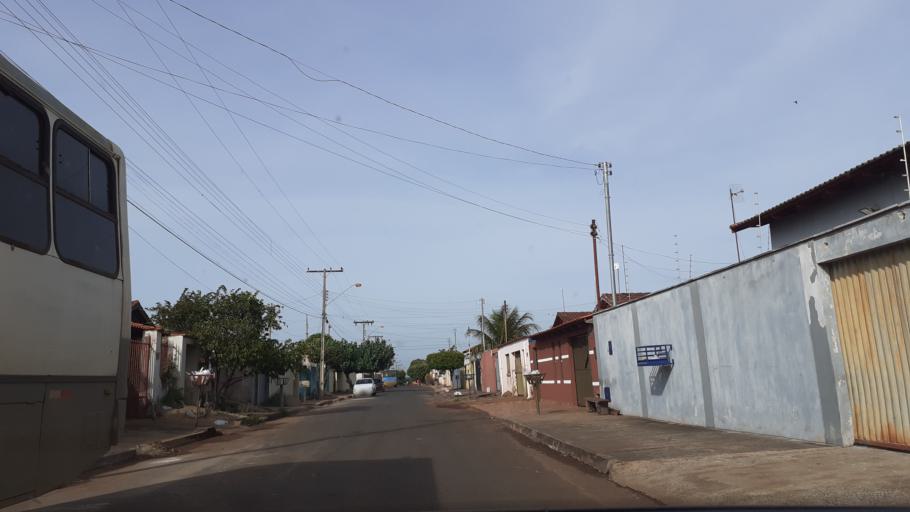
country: BR
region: Goias
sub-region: Itumbiara
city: Itumbiara
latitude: -18.4180
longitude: -49.2466
